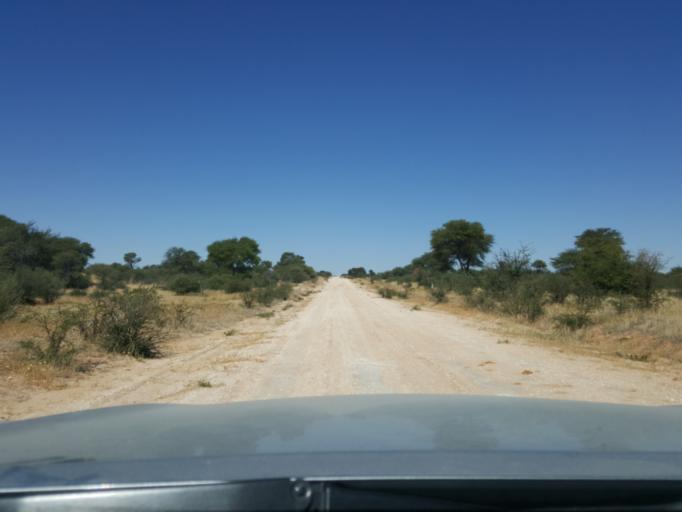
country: BW
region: Kgalagadi
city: Hukuntsi
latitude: -24.0060
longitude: 21.2131
